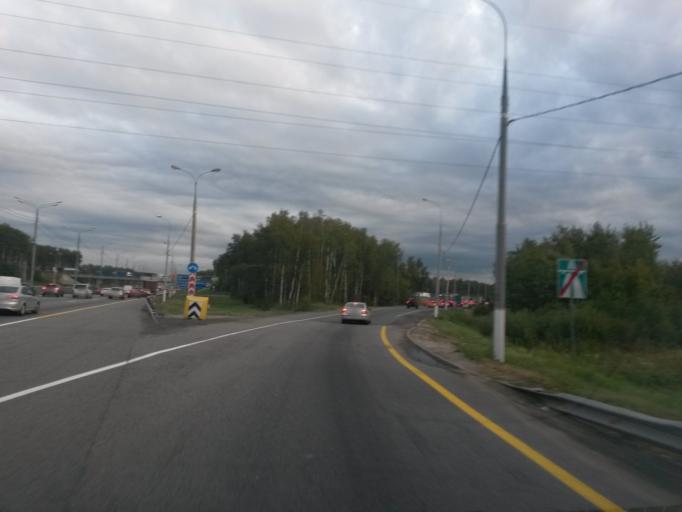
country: RU
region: Moskovskaya
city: Belyye Stolby
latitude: 55.3425
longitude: 37.8076
